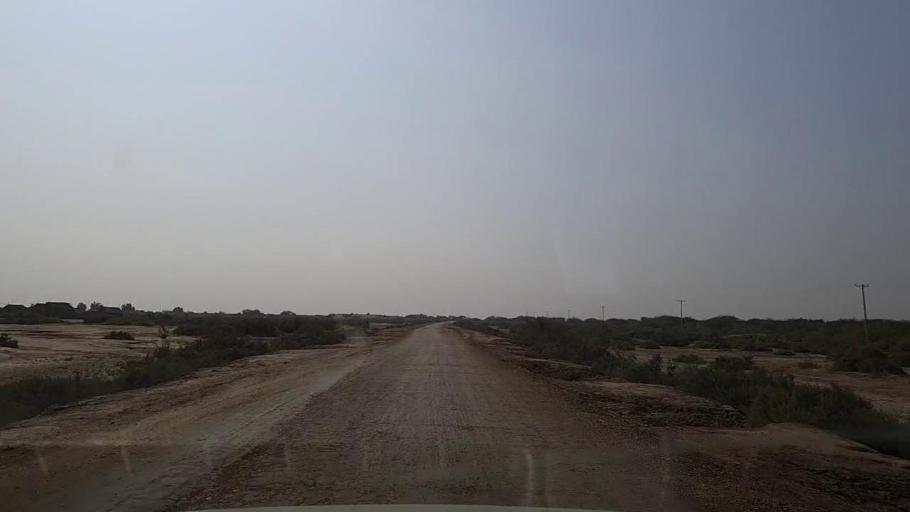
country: PK
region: Sindh
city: Mirpur Sakro
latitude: 24.5324
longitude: 67.5925
